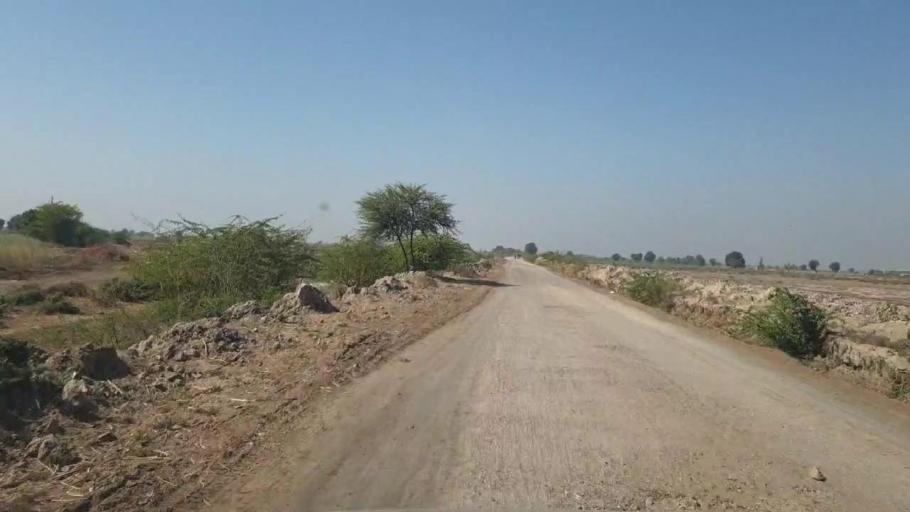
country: PK
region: Sindh
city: Samaro
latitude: 25.2782
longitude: 69.2314
